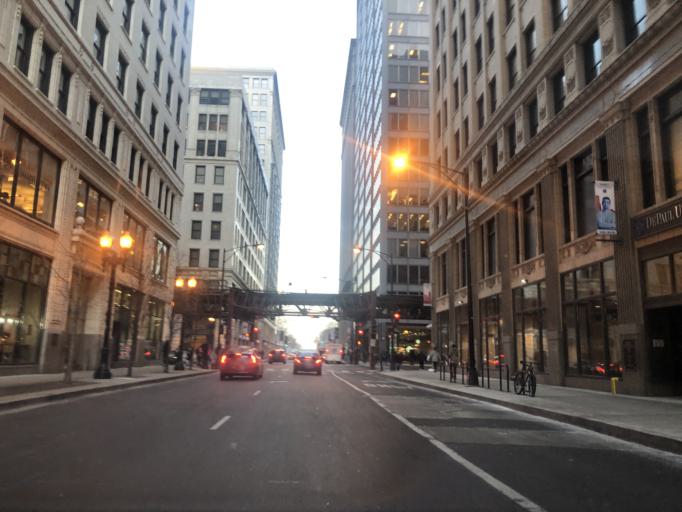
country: US
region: Illinois
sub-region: Cook County
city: Chicago
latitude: 41.8782
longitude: -87.6268
